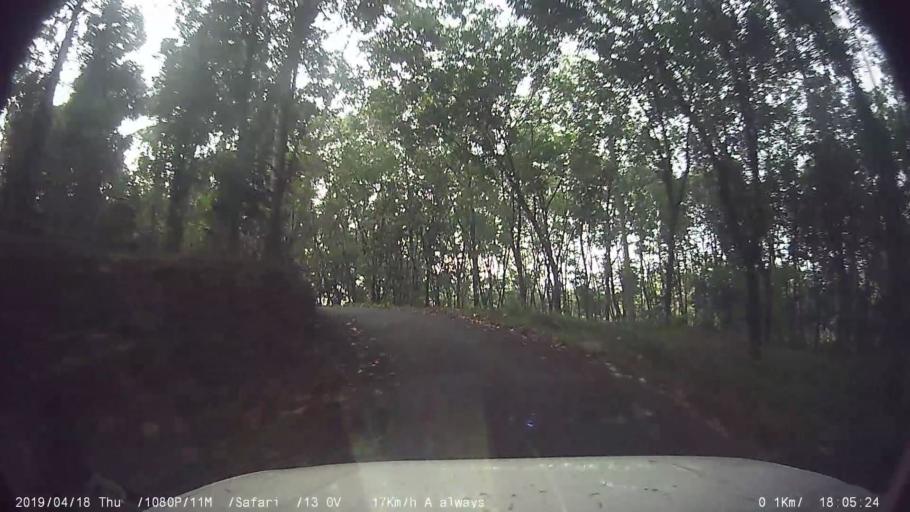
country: IN
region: Kerala
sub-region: Kottayam
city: Palackattumala
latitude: 9.7767
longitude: 76.5922
